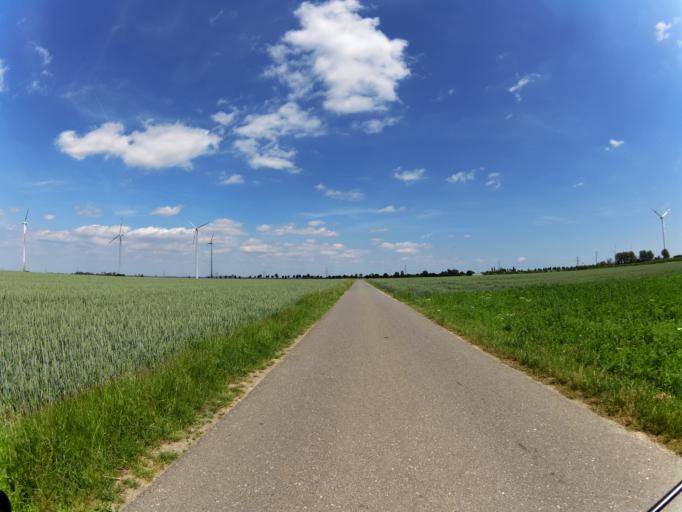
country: DE
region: North Rhine-Westphalia
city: Geilenkirchen
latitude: 51.0136
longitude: 6.1043
